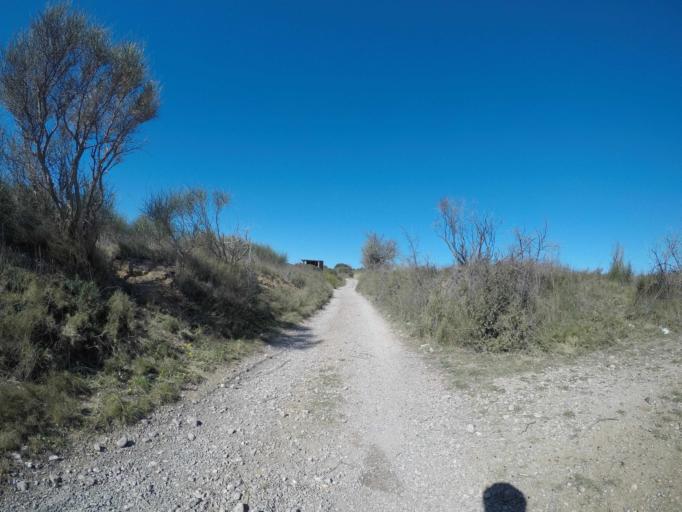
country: FR
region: Languedoc-Roussillon
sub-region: Departement des Pyrenees-Orientales
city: Millas
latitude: 42.7061
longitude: 2.6729
